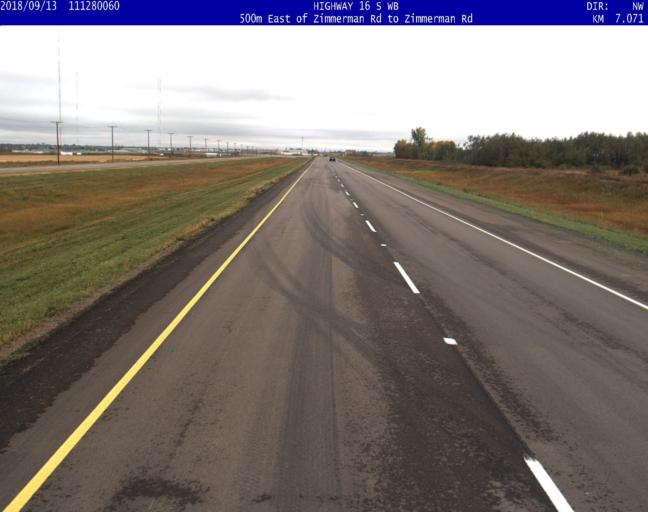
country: CA
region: Saskatchewan
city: Saskatoon
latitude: 52.0749
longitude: -106.5028
